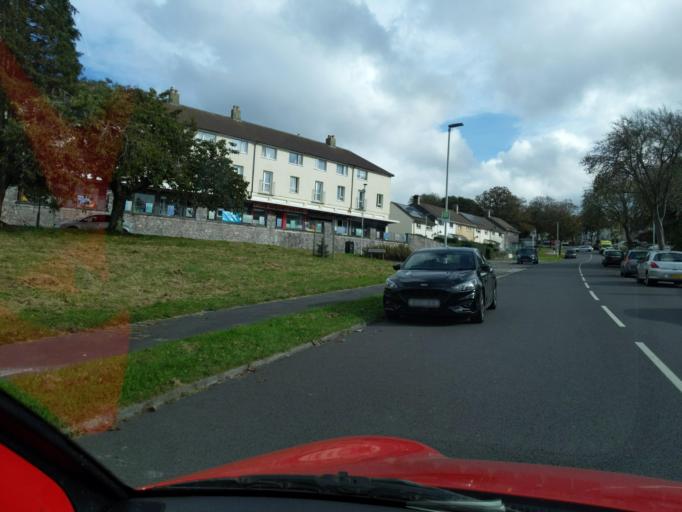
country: GB
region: England
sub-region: Cornwall
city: Torpoint
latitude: 50.4186
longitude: -4.1791
